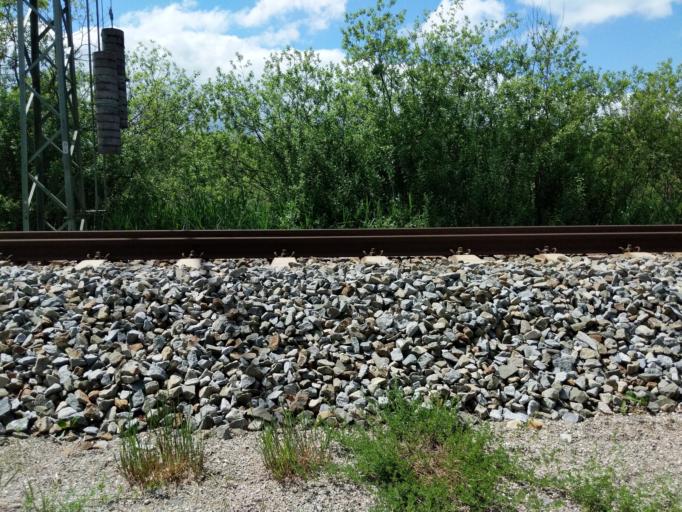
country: DE
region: Bavaria
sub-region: Upper Bavaria
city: Herrsching am Ammersee
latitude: 48.0122
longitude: 11.1727
